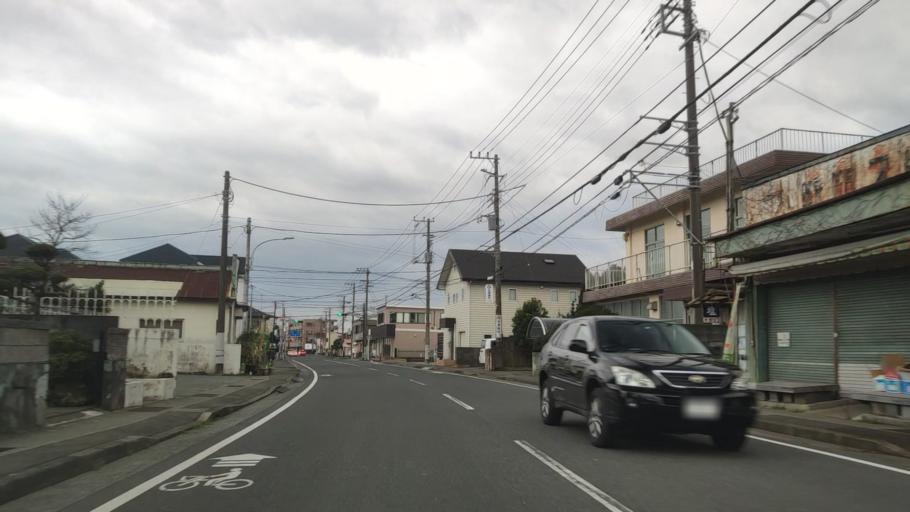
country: JP
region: Kanagawa
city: Odawara
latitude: 35.2694
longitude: 139.1894
